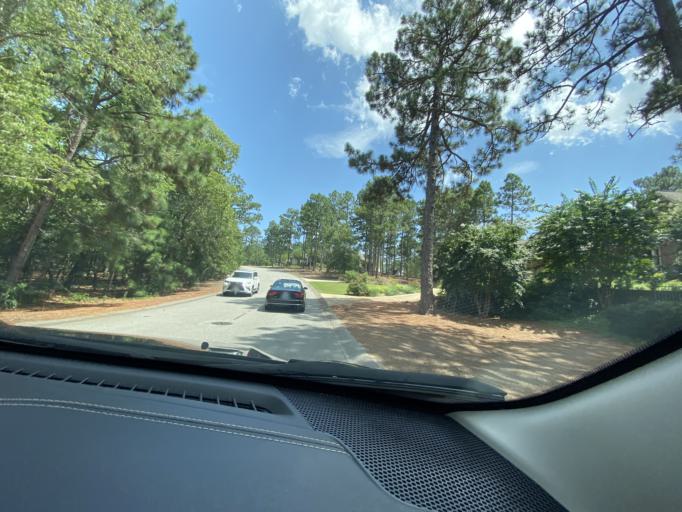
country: US
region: North Carolina
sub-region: Moore County
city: Pinehurst
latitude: 35.1978
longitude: -79.4339
